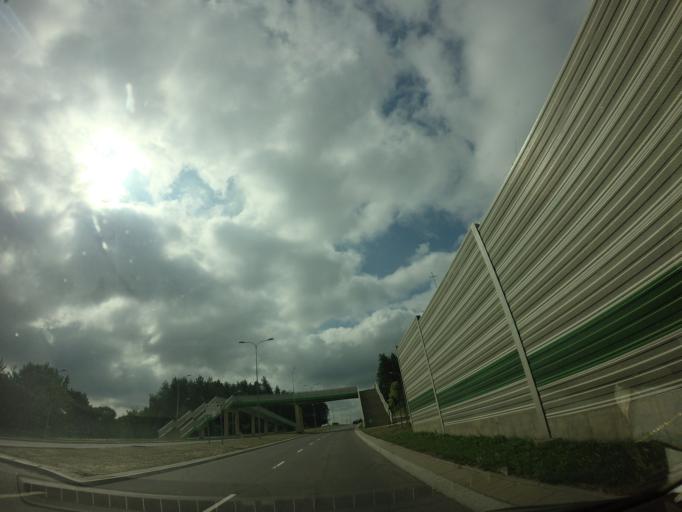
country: PL
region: Podlasie
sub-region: Bialystok
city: Bialystok
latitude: 53.1341
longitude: 23.2214
